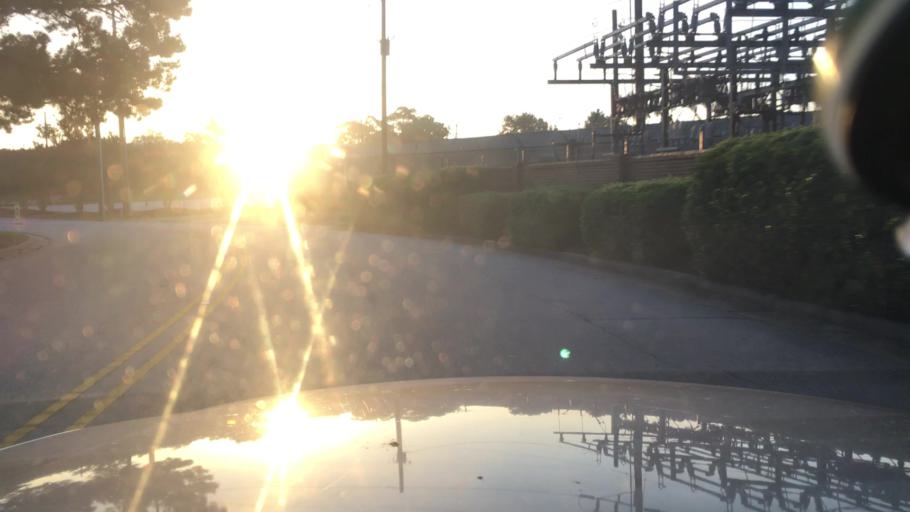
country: US
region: North Carolina
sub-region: Cumberland County
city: Fayetteville
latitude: 35.0657
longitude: -78.9254
